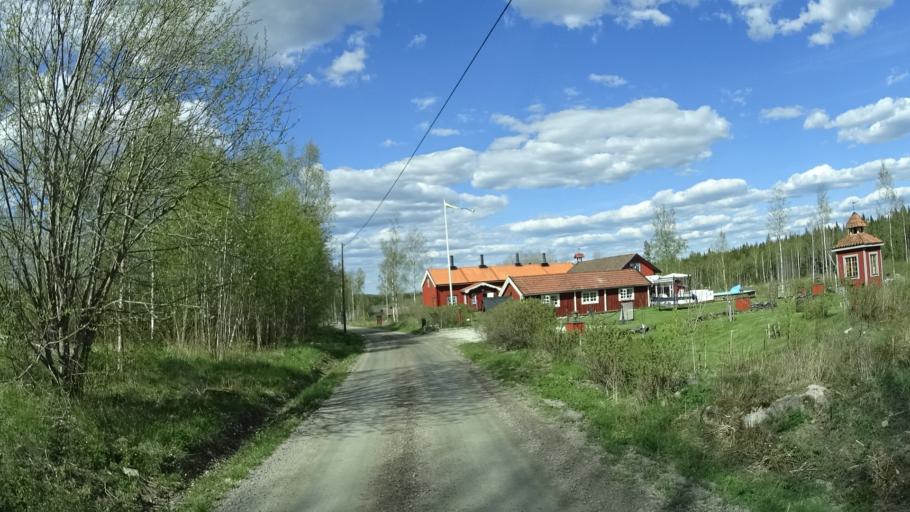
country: SE
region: OErebro
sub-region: Orebro Kommun
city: Garphyttan
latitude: 59.4241
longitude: 14.8658
